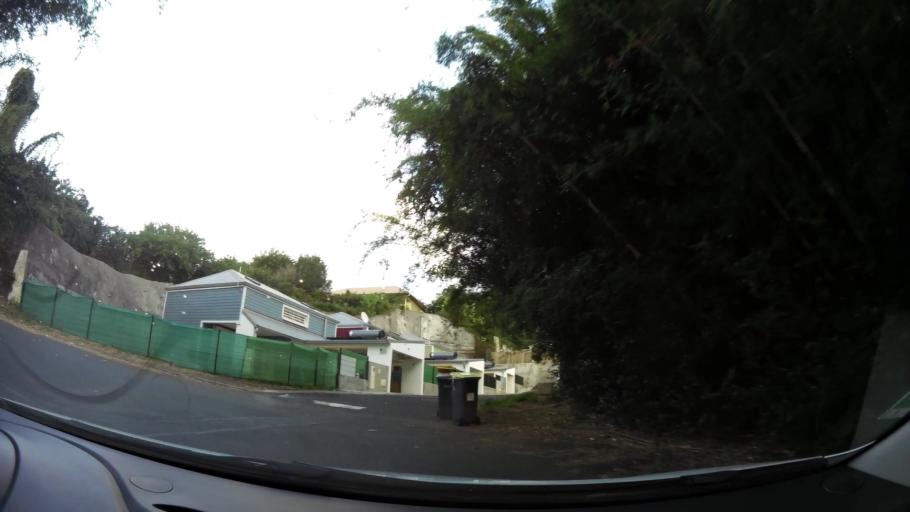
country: RE
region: Reunion
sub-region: Reunion
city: Saint-Denis
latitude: -20.9199
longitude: 55.4375
